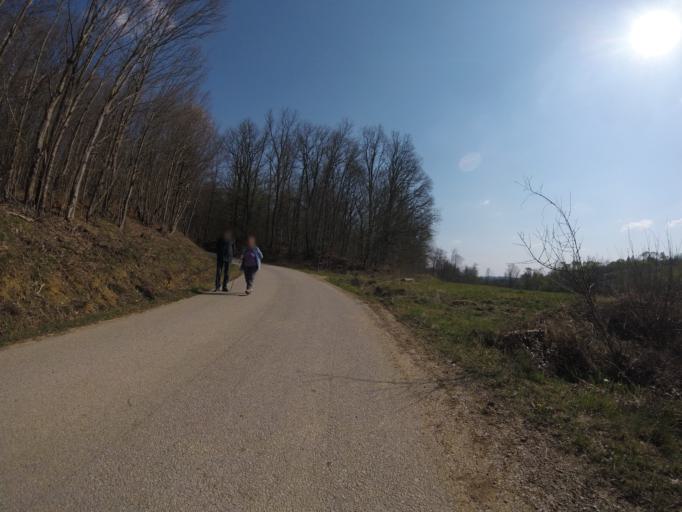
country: HR
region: Sisacko-Moslavacka
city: Gvozd
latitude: 45.5142
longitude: 15.9280
